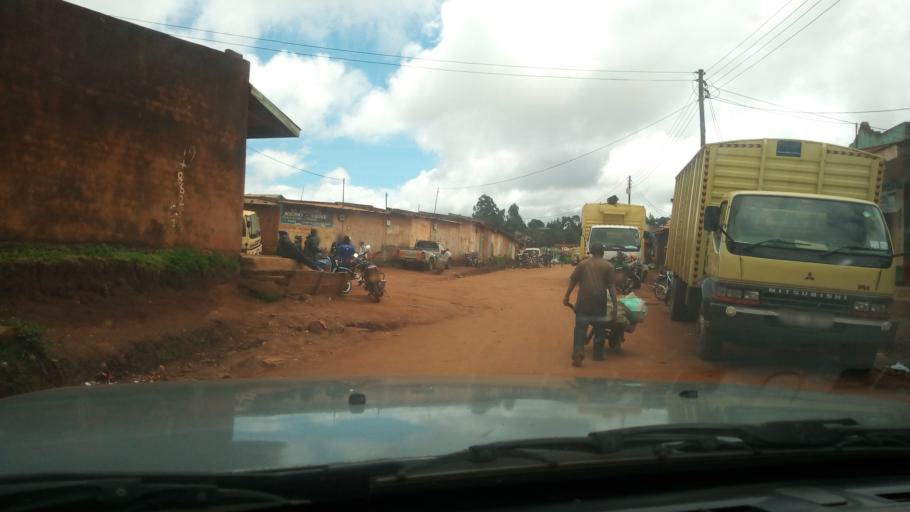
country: KE
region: Makueni
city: Wote
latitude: -1.6633
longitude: 37.4468
